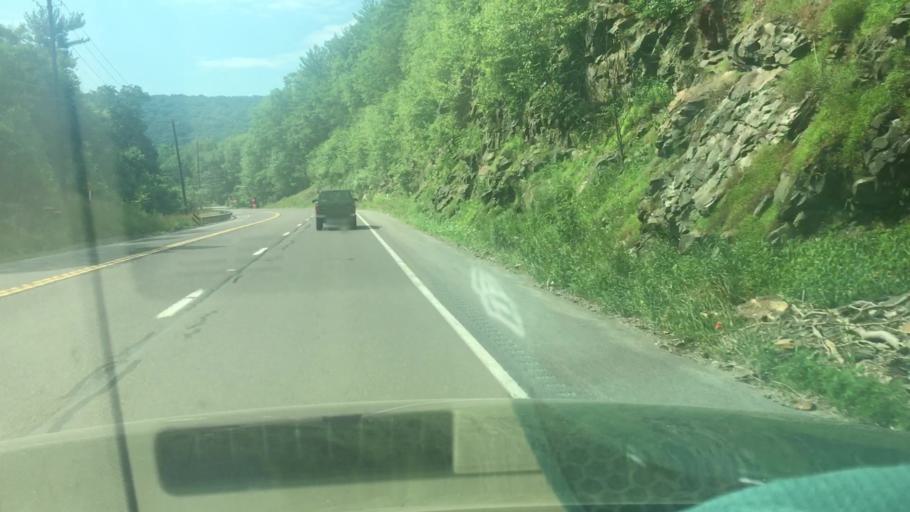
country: US
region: Pennsylvania
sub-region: Northumberland County
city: Kulpmont
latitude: 40.8259
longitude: -76.5029
